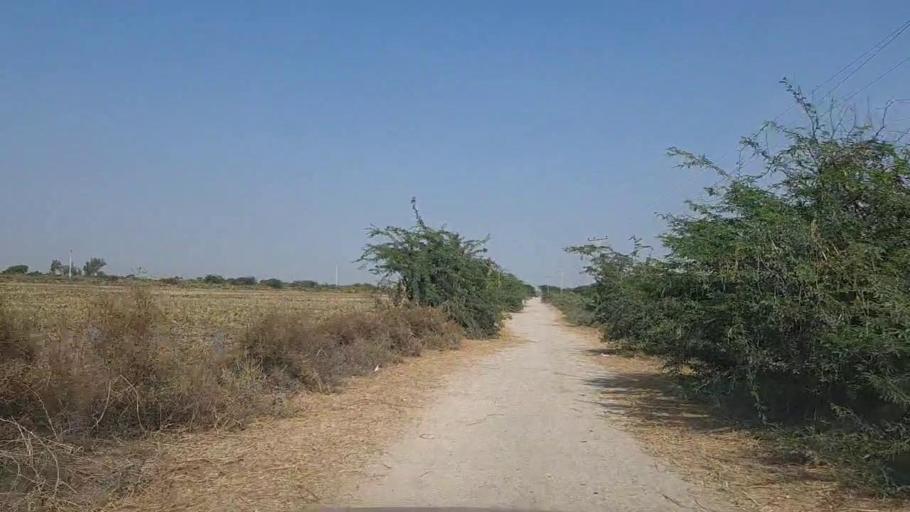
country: PK
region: Sindh
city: Thatta
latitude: 24.6004
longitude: 67.9522
